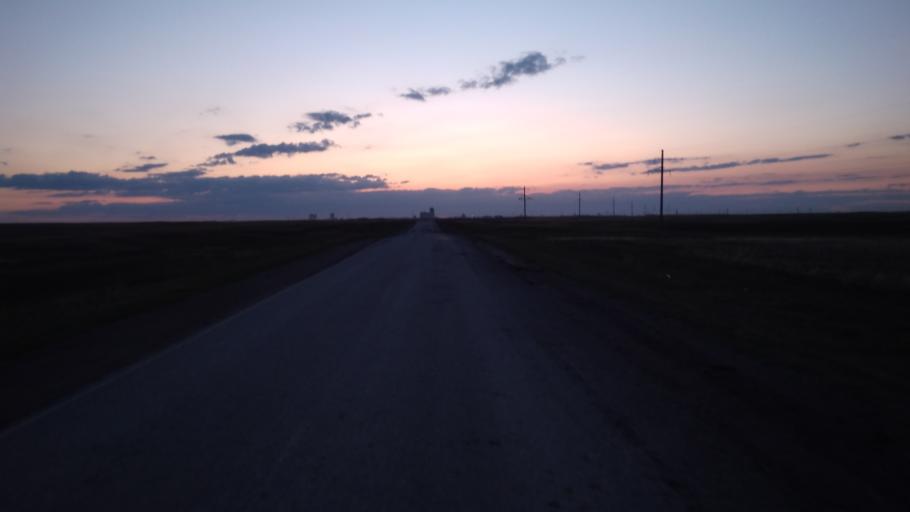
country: RU
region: Chelyabinsk
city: Troitsk
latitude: 54.0919
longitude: 61.6419
